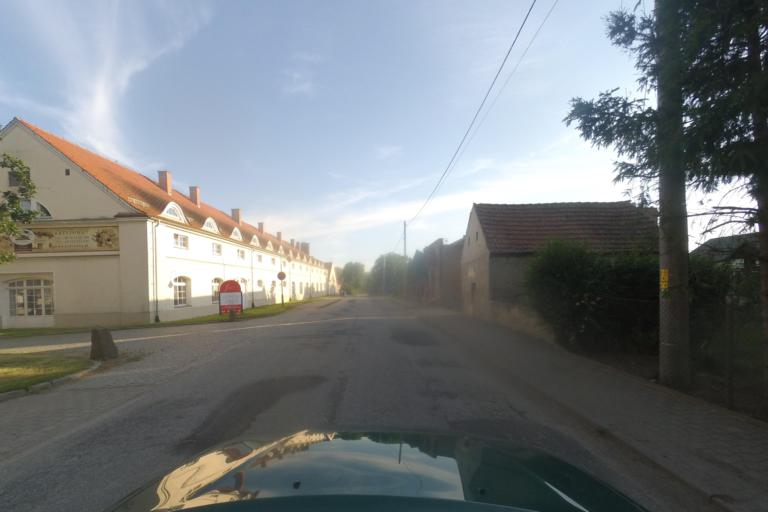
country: PL
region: Lower Silesian Voivodeship
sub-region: Powiat swidnicki
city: Swidnica
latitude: 50.7982
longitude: 16.5333
